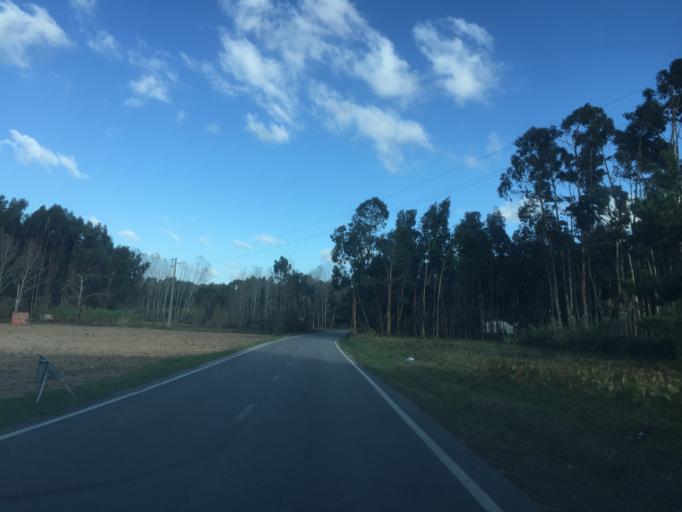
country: PT
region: Coimbra
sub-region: Figueira da Foz
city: Buarcos
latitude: 40.2150
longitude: -8.8832
